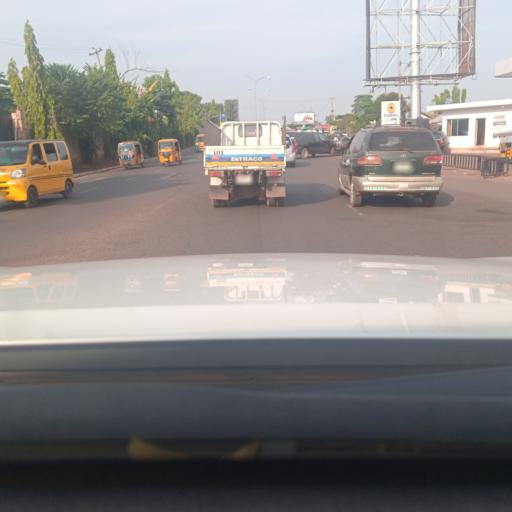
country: NG
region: Enugu
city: Enugu
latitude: 6.4492
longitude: 7.5011
